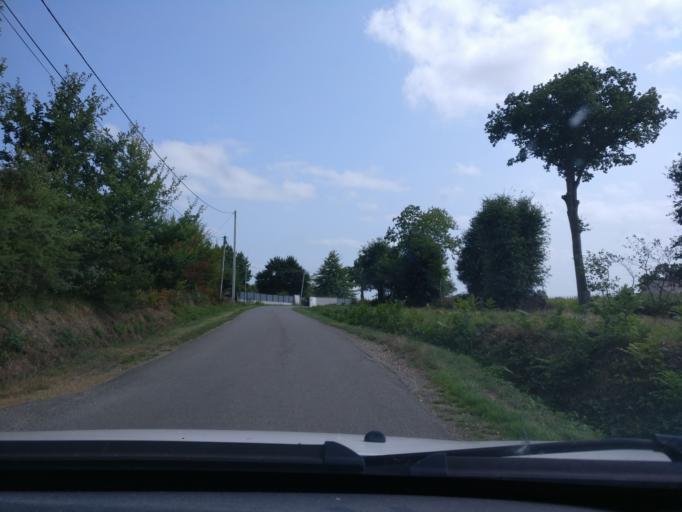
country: FR
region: Brittany
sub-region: Departement d'Ille-et-Vilaine
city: Erce-pres-Liffre
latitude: 48.2668
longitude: -1.5284
